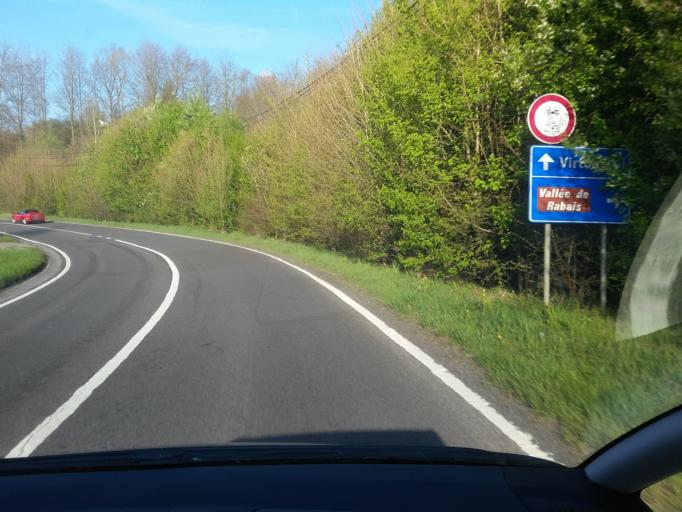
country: BE
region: Wallonia
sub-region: Province du Luxembourg
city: Virton
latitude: 49.5807
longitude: 5.5556
